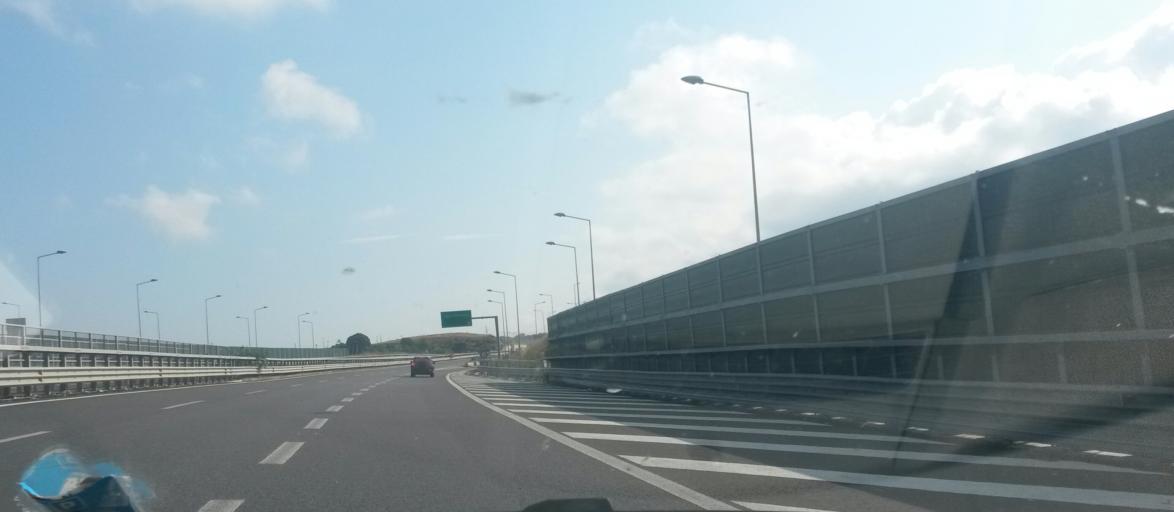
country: IT
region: Calabria
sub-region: Provincia di Reggio Calabria
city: Campo Calabro
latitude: 38.2075
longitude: 15.6415
